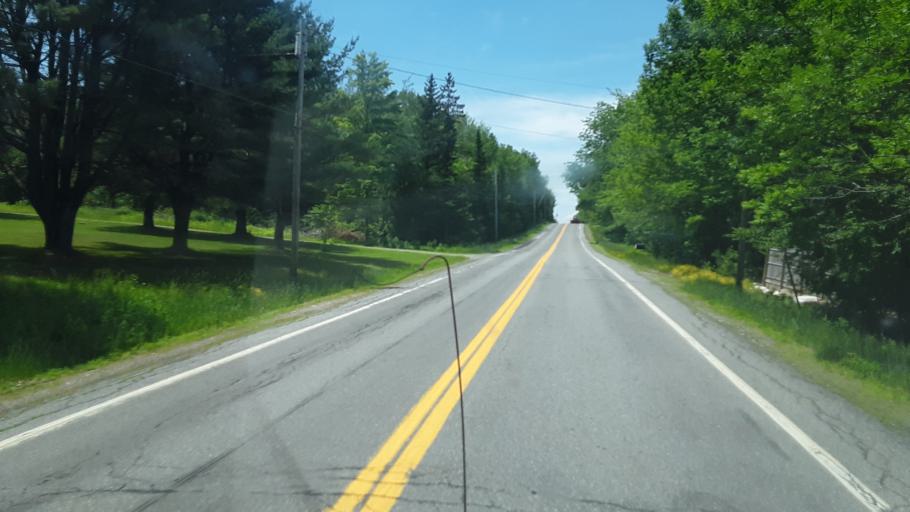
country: US
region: Maine
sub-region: Hancock County
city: Bucksport
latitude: 44.5678
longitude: -68.8304
